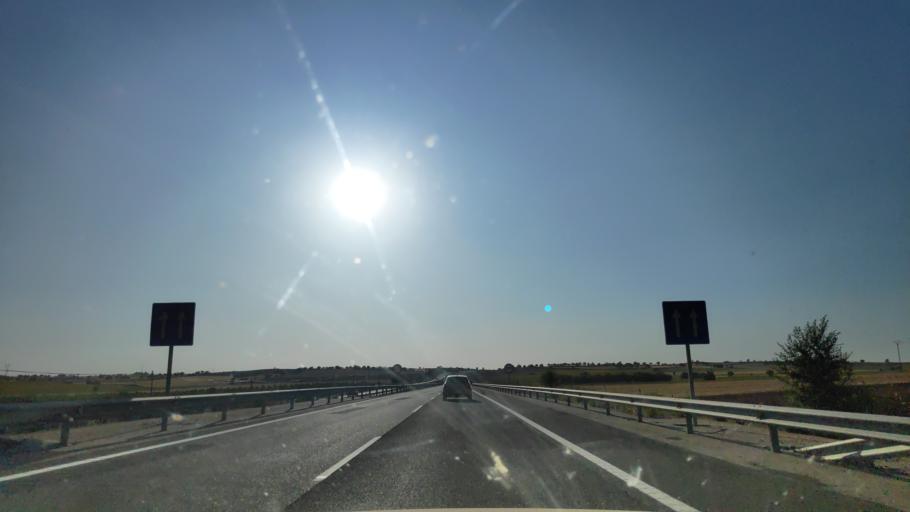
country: ES
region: Castille-La Mancha
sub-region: Provincia de Cuenca
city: Saelices
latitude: 39.9313
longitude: -2.8492
